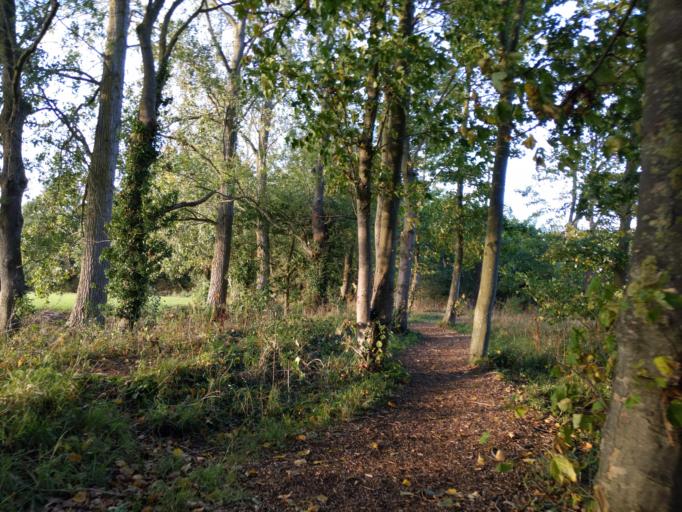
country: GB
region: England
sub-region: Oxfordshire
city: Radley
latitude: 51.6978
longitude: -1.2474
